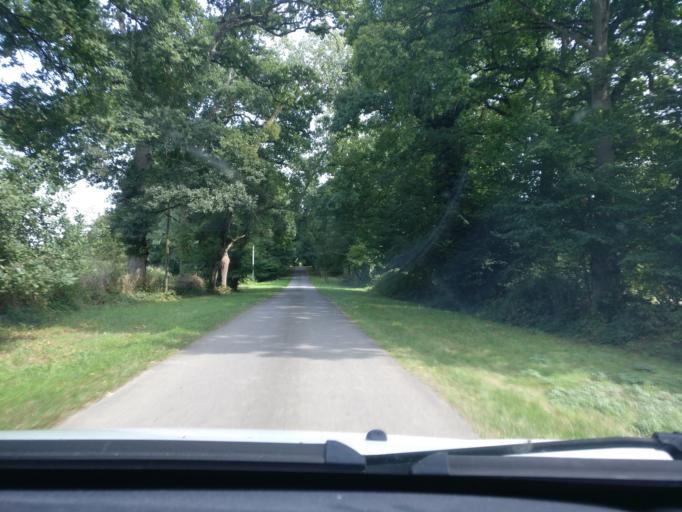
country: FR
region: Brittany
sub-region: Departement d'Ille-et-Vilaine
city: Erce-pres-Liffre
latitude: 48.2604
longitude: -1.5127
